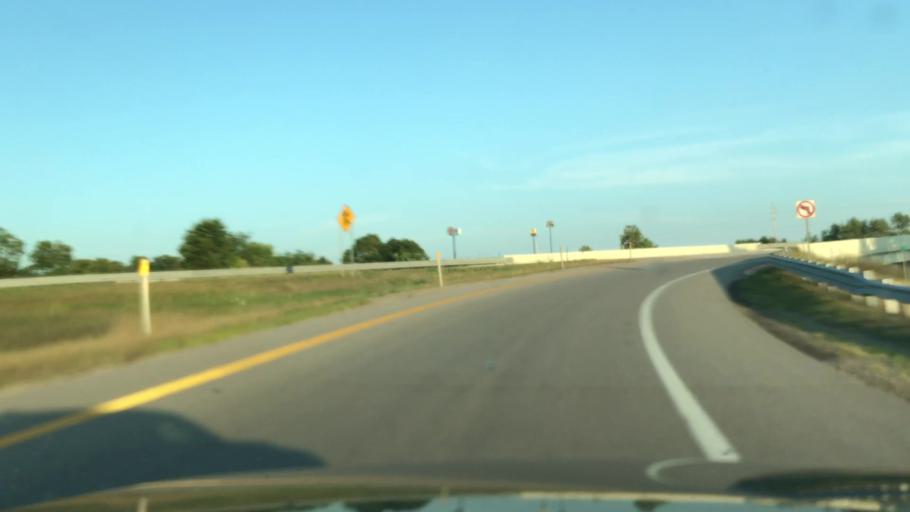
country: US
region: Michigan
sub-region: Osceola County
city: Reed City
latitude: 43.8908
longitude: -85.5287
